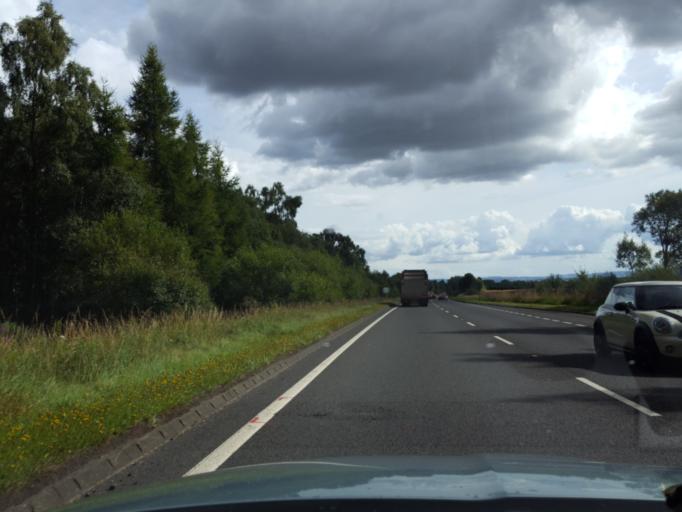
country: GB
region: Scotland
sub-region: Perth and Kinross
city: Bankfoot
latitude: 56.5099
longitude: -3.5126
